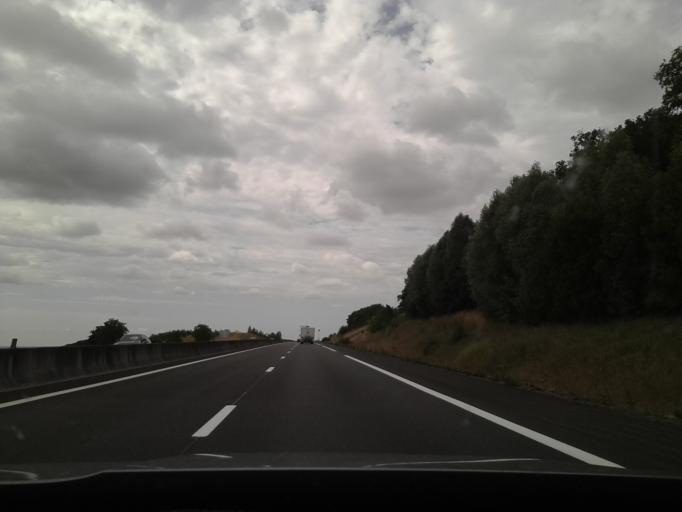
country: FR
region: Pays de la Loire
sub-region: Departement de la Sarthe
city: Arconnay
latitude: 48.3757
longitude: 0.1032
